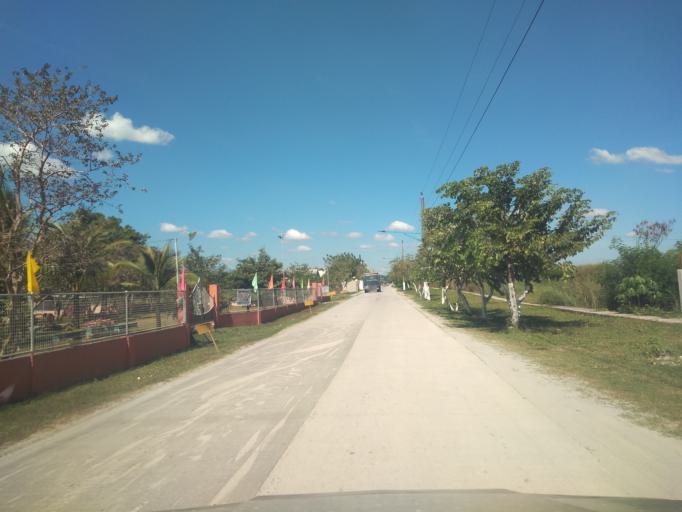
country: PH
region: Central Luzon
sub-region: Province of Pampanga
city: Balas
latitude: 15.0383
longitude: 120.6190
